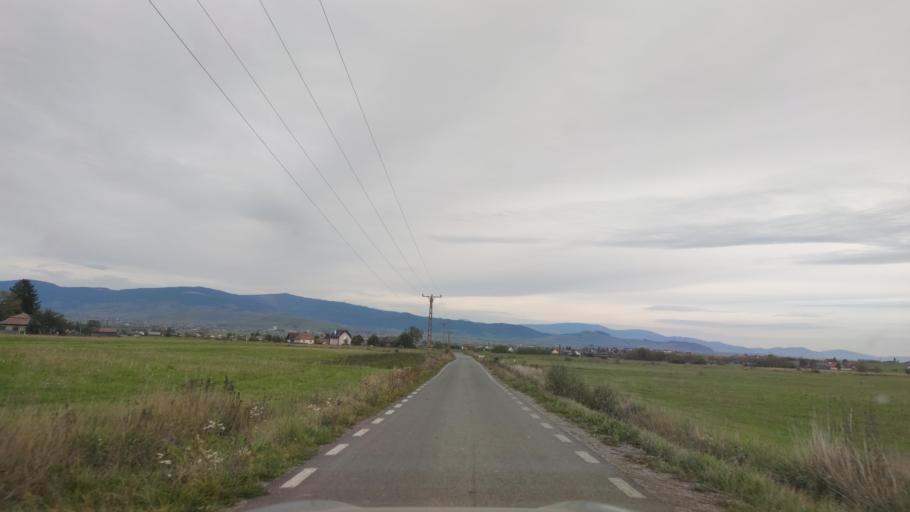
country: RO
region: Harghita
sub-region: Comuna Remetea
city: Remetea
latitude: 46.8086
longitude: 25.4300
